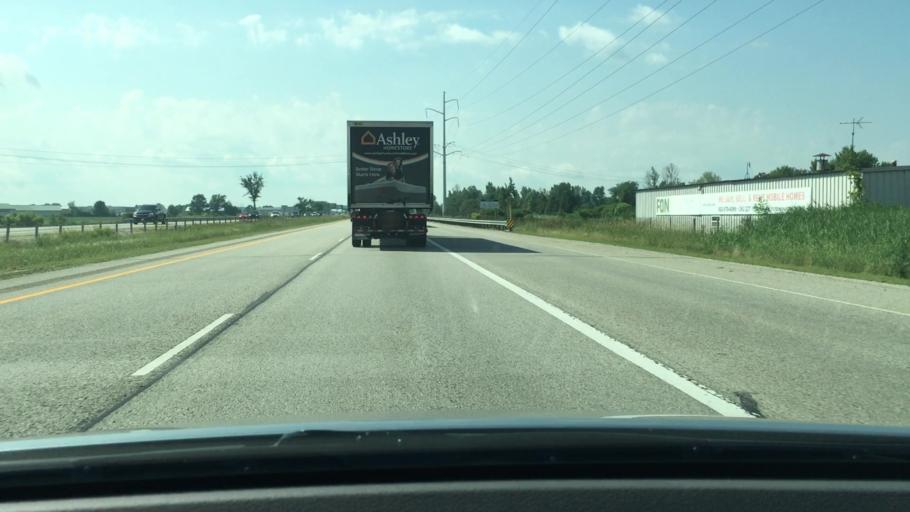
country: US
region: Wisconsin
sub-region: Fond du Lac County
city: North Fond du Lac
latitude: 43.8083
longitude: -88.5023
